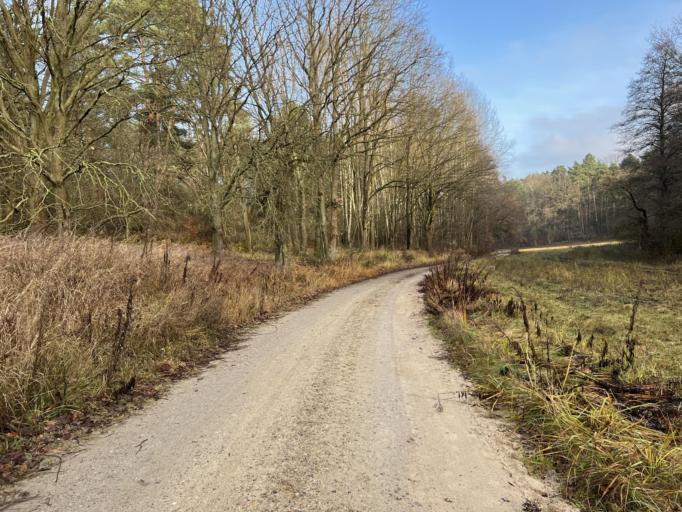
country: DE
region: Brandenburg
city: Eberswalde
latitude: 52.8328
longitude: 13.8716
